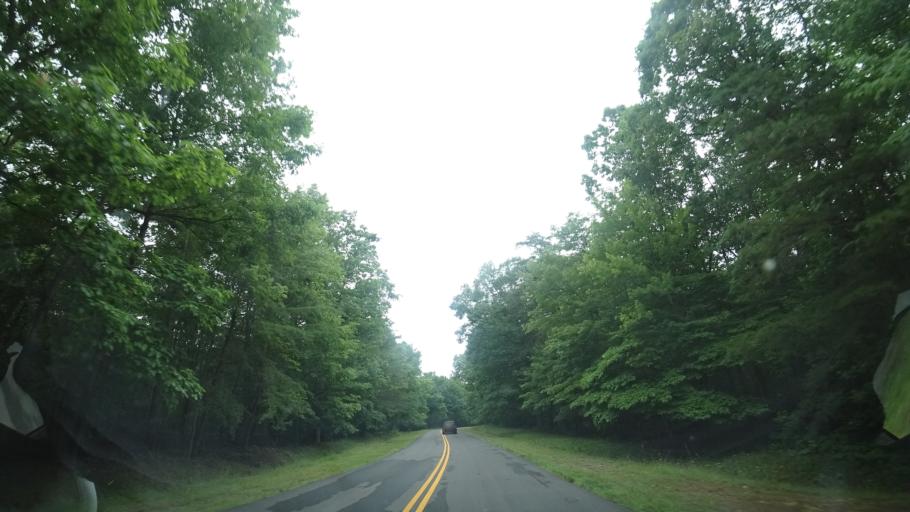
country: US
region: Virginia
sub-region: Louisa County
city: Louisa
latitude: 38.1292
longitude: -77.8195
